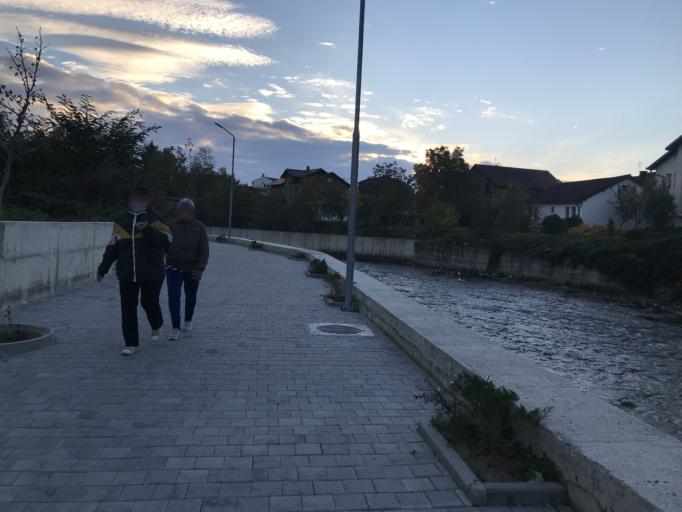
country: XK
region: Pec
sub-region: Komuna e Pejes
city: Peje
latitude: 42.6589
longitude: 20.2775
